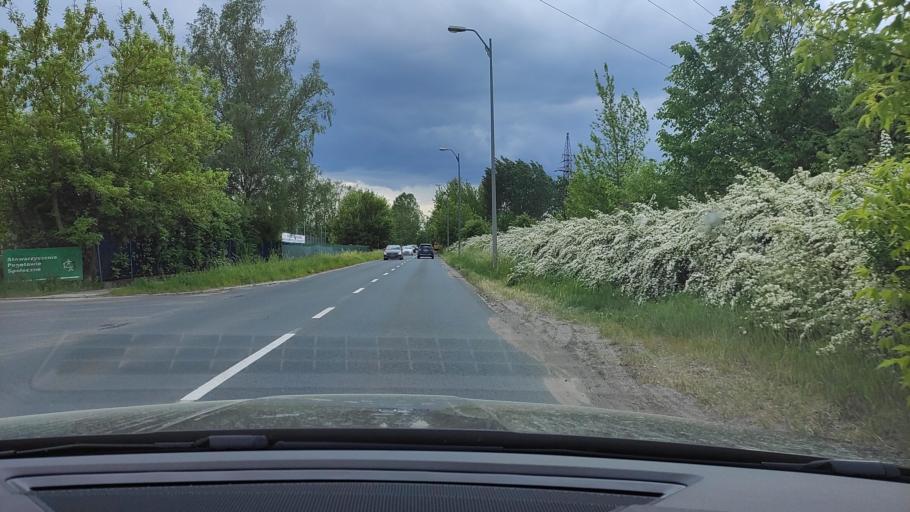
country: PL
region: Greater Poland Voivodeship
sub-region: Powiat poznanski
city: Swarzedz
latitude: 52.3892
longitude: 17.0311
